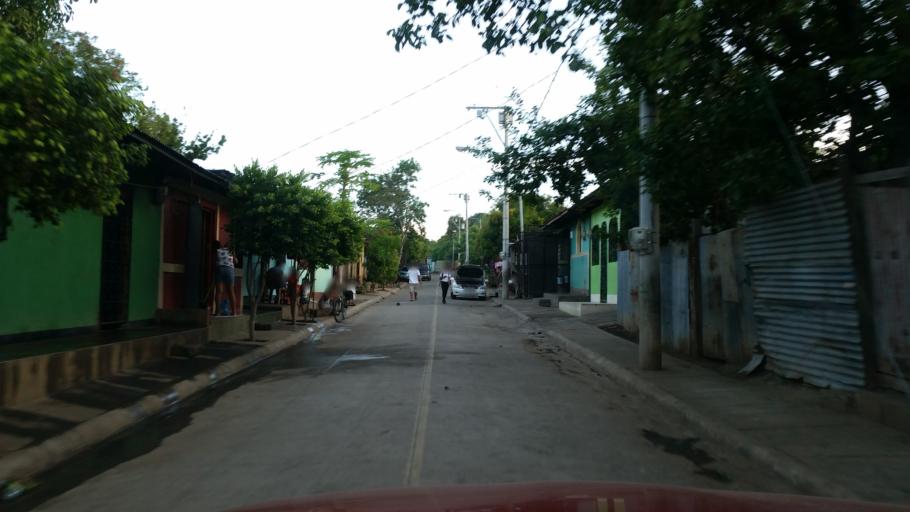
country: NI
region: Managua
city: Managua
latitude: 12.1293
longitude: -86.2880
